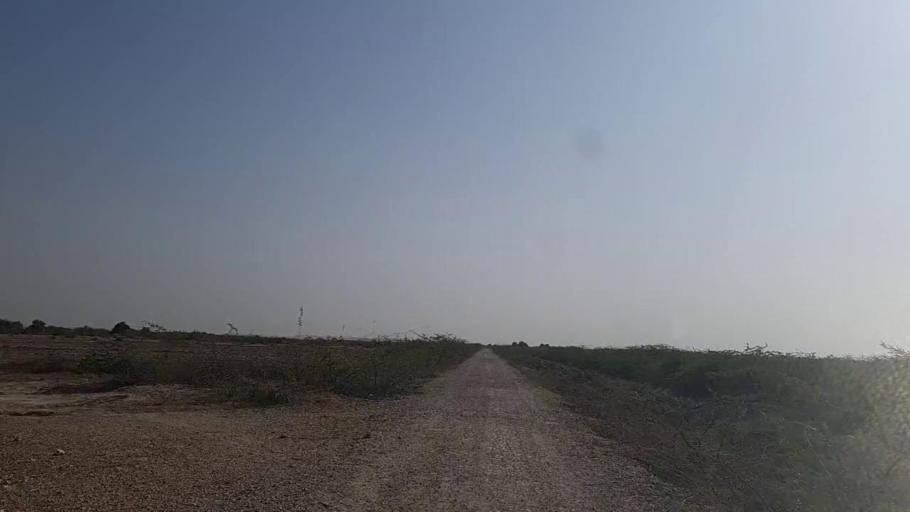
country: PK
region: Sindh
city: Naukot
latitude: 24.5972
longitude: 69.2637
